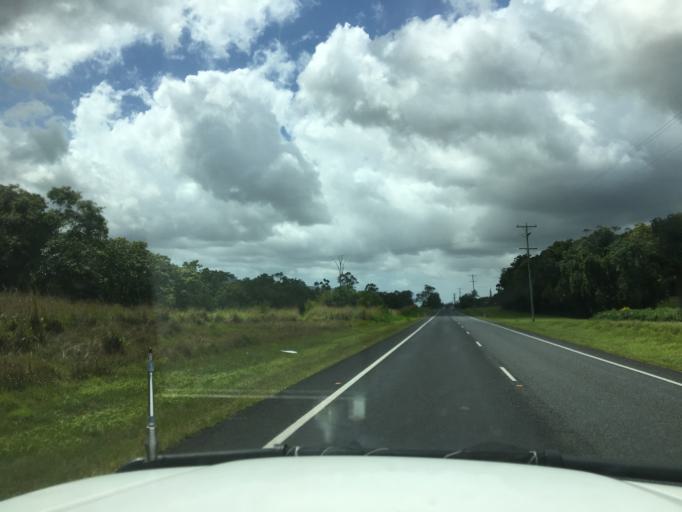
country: AU
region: Queensland
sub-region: Cairns
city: Woree
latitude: -17.1476
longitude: 145.8531
